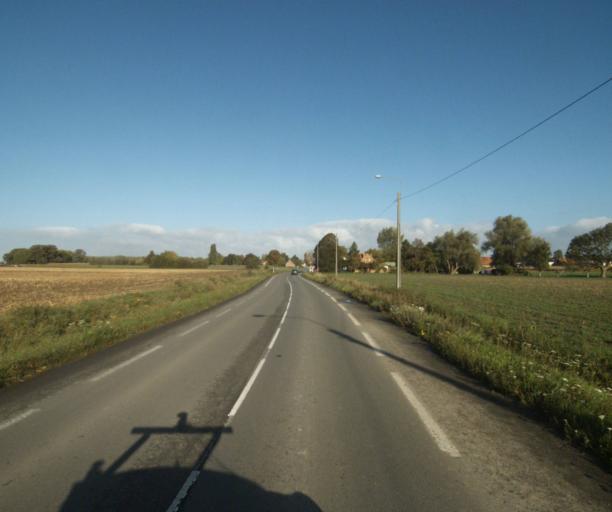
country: FR
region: Nord-Pas-de-Calais
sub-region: Departement du Nord
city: Verlinghem
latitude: 50.6754
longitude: 3.0012
